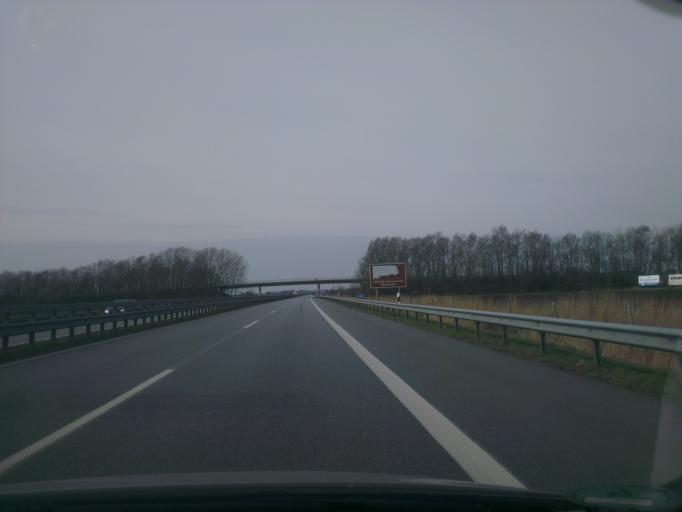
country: DE
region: Lower Saxony
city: Emden
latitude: 53.3646
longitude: 7.2740
